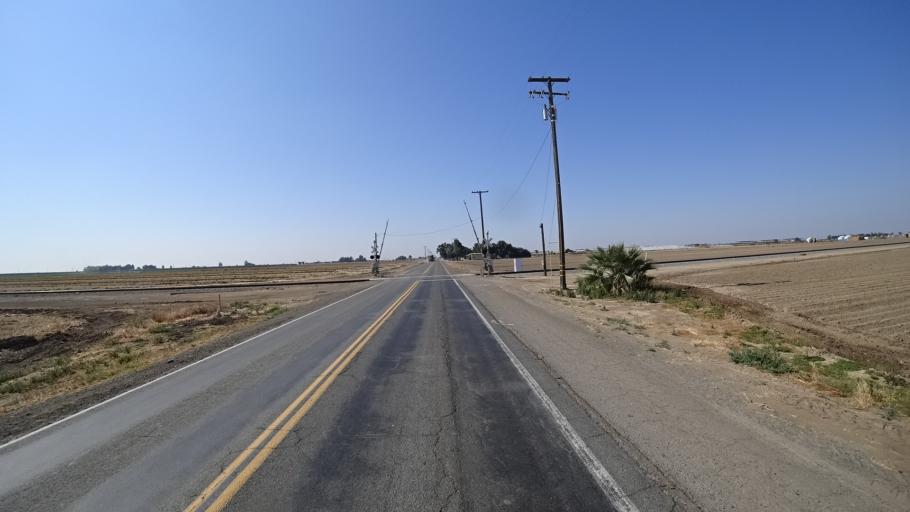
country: US
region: California
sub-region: Kings County
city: Home Garden
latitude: 36.3378
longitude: -119.5651
